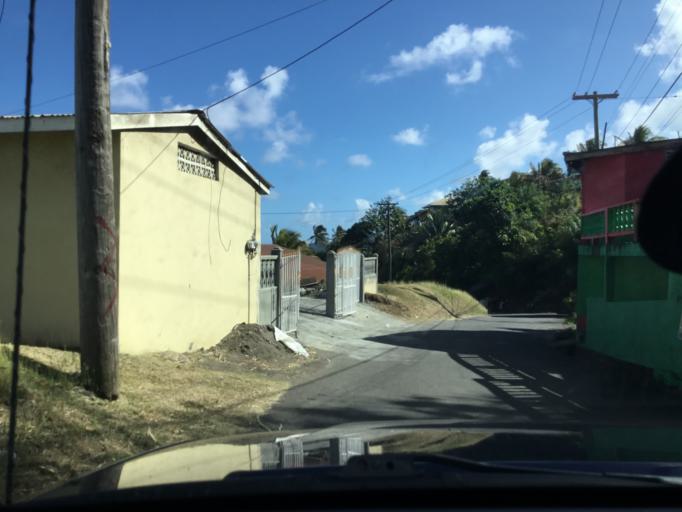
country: VC
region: Charlotte
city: Biabou
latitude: 13.1566
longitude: -61.1577
